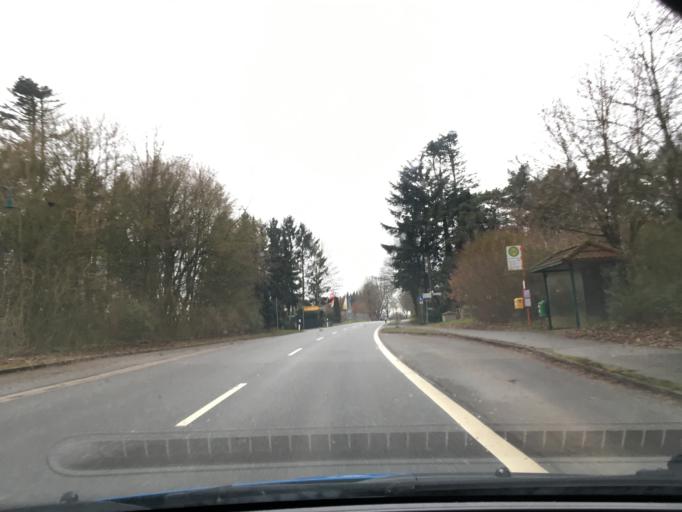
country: DE
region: Schleswig-Holstein
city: Hornbek
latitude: 53.5649
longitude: 10.6437
